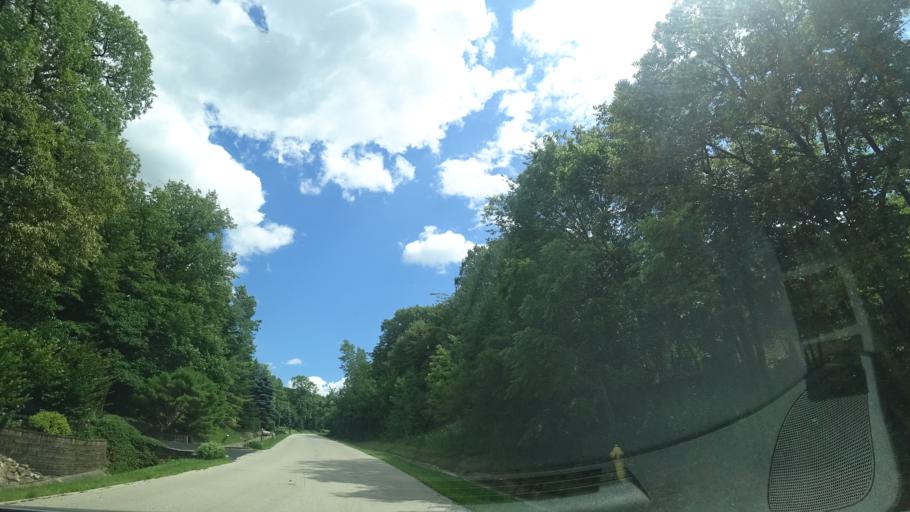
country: US
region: Illinois
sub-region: Will County
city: Homer Glen
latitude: 41.5885
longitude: -87.9176
